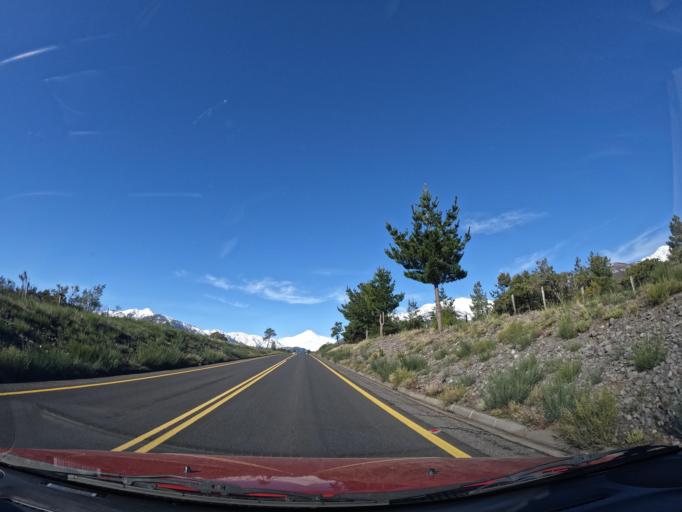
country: CL
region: Biobio
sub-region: Provincia de Biobio
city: Mulchen
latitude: -37.3427
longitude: -71.5907
